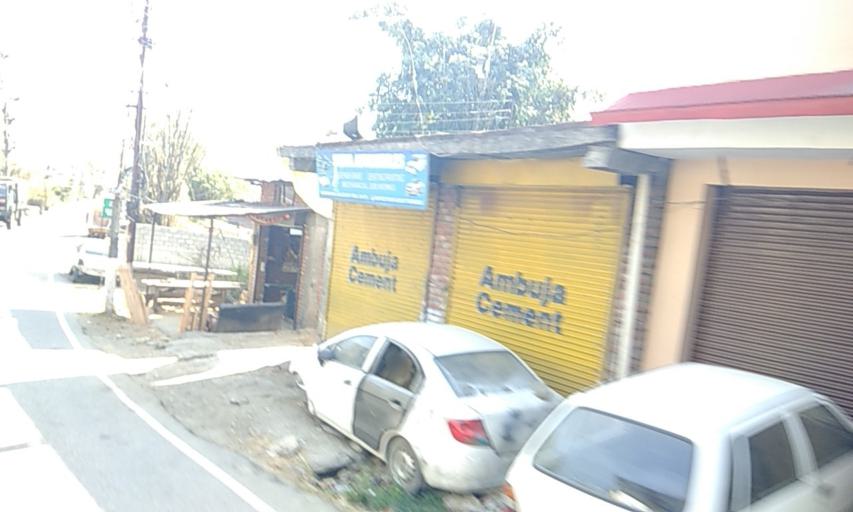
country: IN
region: Himachal Pradesh
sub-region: Kangra
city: Dharmsala
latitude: 32.1706
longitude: 76.3902
